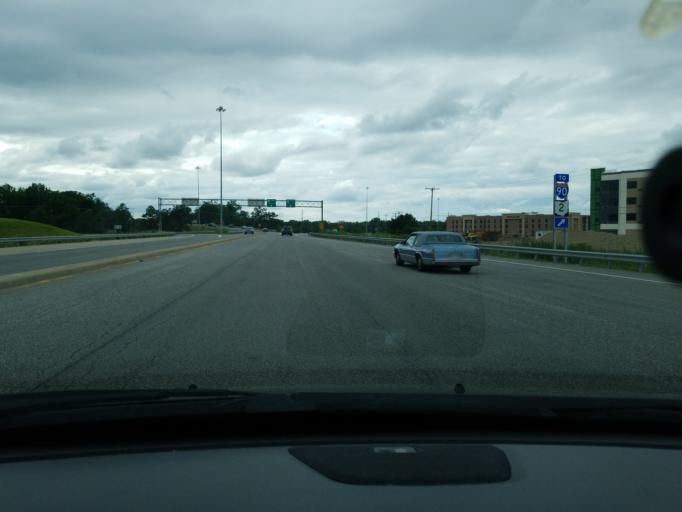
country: US
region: Ohio
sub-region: Lorain County
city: Elyria
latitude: 41.3902
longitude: -82.1131
